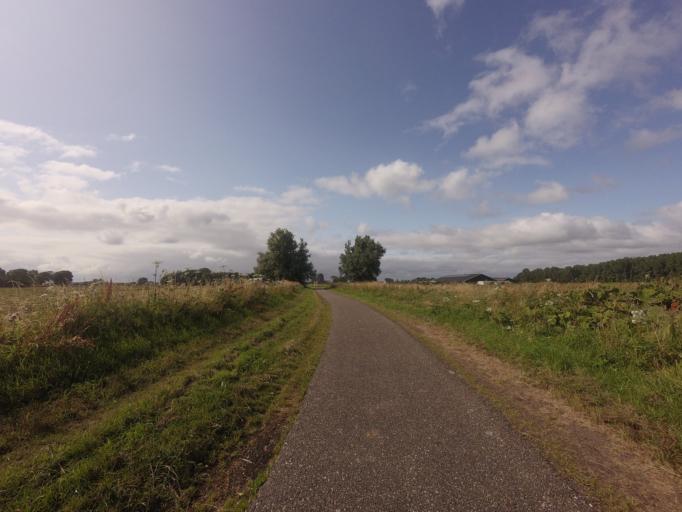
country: NL
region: North Holland
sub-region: Gemeente Haarlem
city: Haarlem
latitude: 52.4007
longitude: 4.6990
